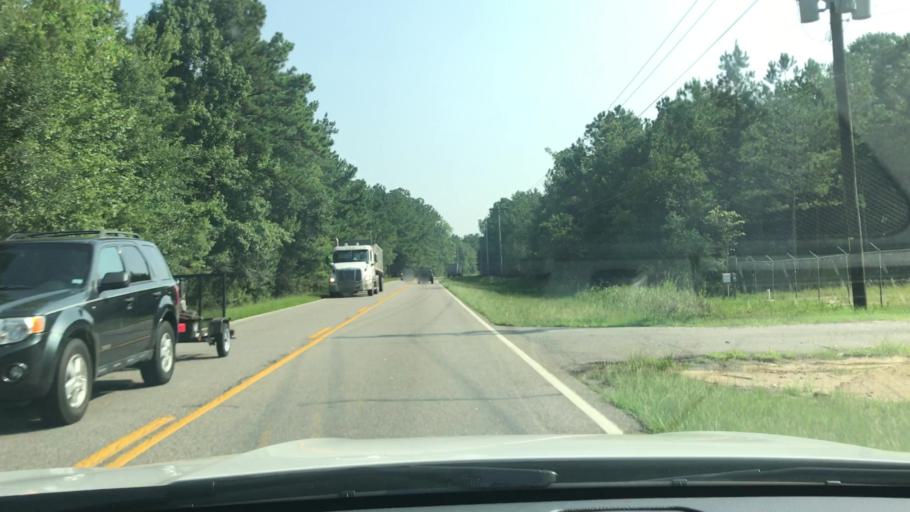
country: US
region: South Carolina
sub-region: Georgetown County
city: Georgetown
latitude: 33.5230
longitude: -79.2444
